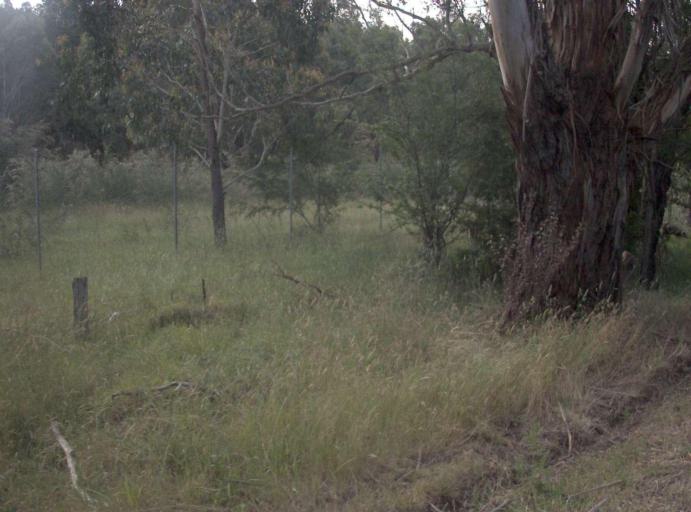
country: AU
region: Victoria
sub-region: Latrobe
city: Morwell
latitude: -38.1989
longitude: 146.4022
